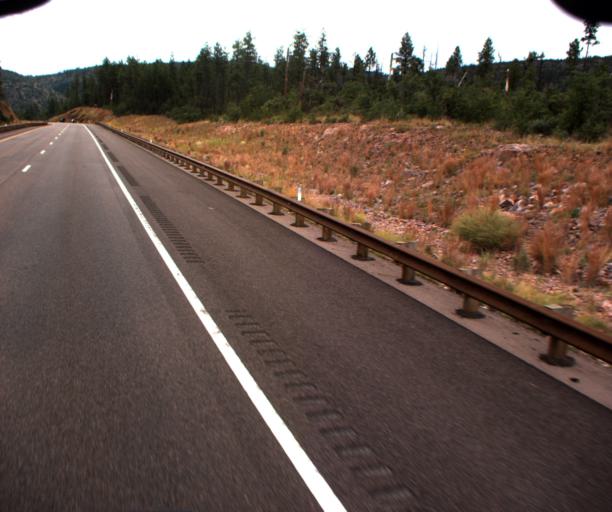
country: US
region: Arizona
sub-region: Gila County
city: Star Valley
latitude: 34.3151
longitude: -111.0581
